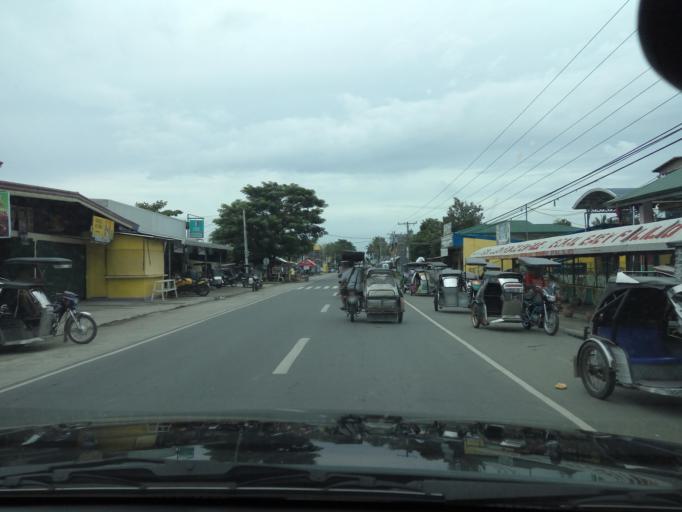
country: PH
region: Central Luzon
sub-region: Province of Nueva Ecija
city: Concepcion
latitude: 15.4491
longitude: 120.8004
